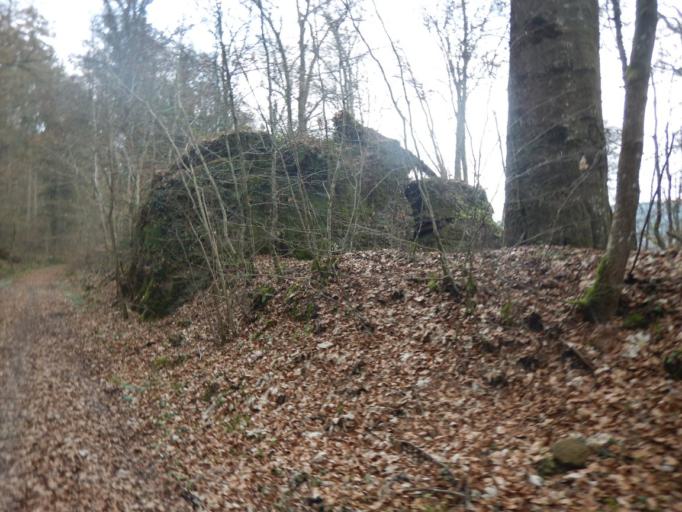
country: LU
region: Grevenmacher
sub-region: Canton d'Echternach
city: Beaufort
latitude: 49.8404
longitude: 6.3177
